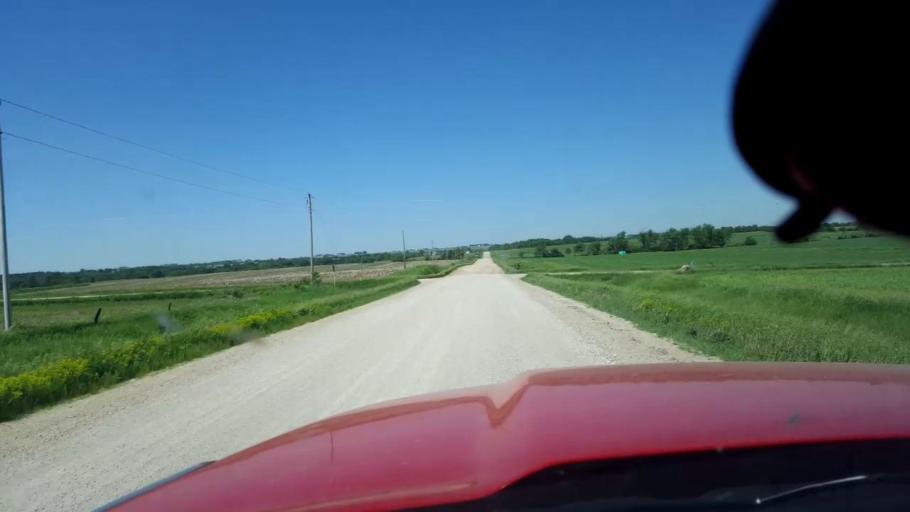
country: US
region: Iowa
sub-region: Chickasaw County
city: New Hampton
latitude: 43.2135
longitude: -92.2582
